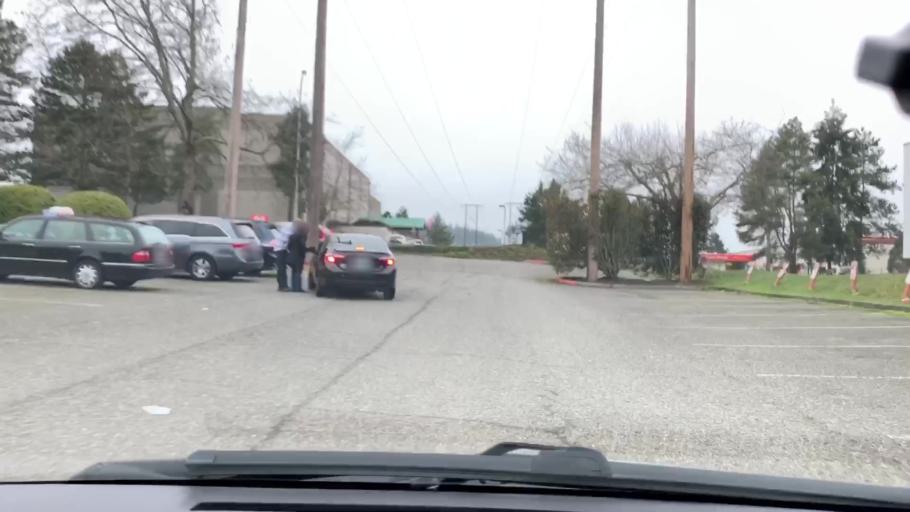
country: US
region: Washington
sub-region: King County
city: Bellevue
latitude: 47.6225
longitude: -122.1591
